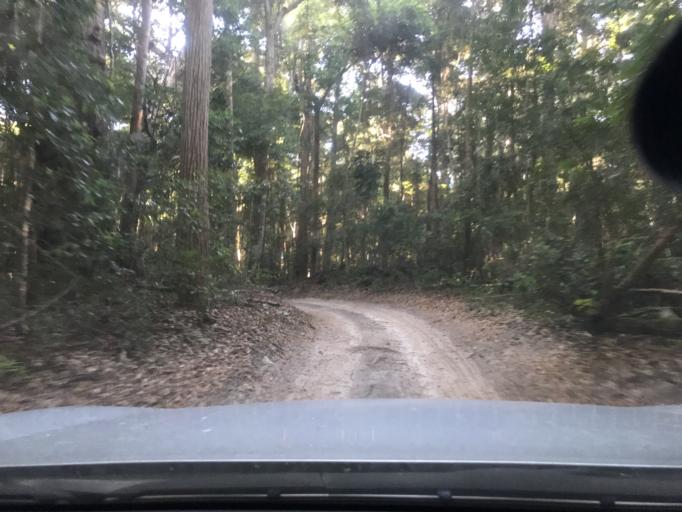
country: AU
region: Queensland
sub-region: Fraser Coast
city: Urangan
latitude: -25.3251
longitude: 153.1508
